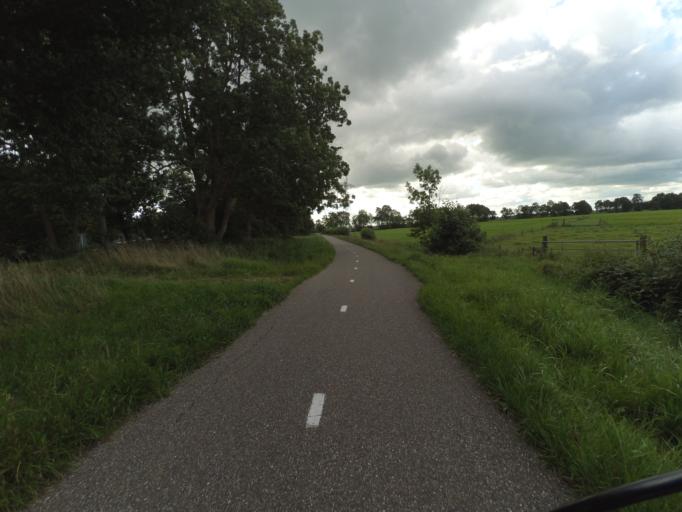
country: NL
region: Friesland
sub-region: Gemeente Tytsjerksteradiel
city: Hurdegaryp
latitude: 53.2088
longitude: 5.9414
